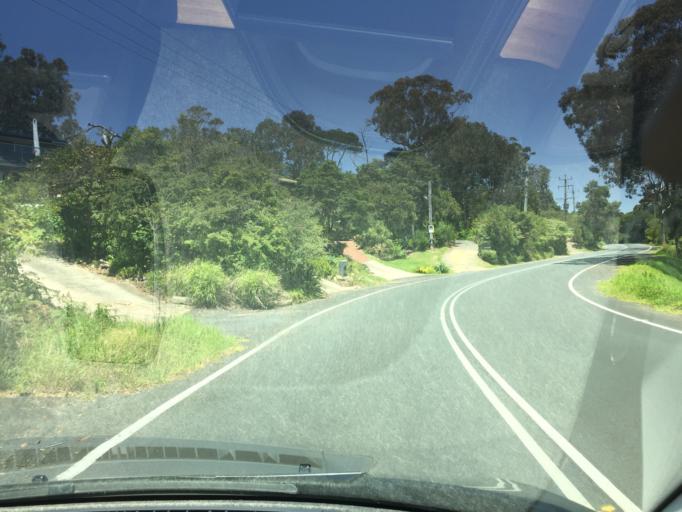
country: AU
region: New South Wales
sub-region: Bega Valley
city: Merimbula
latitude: -36.8896
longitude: 149.9248
